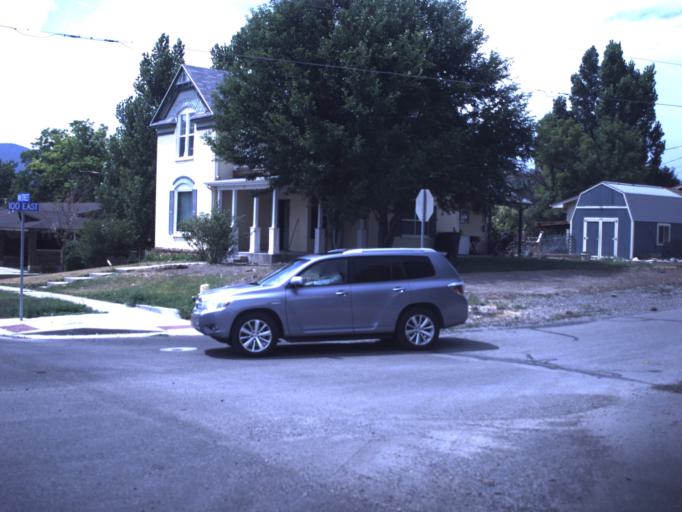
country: US
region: Utah
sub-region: Sanpete County
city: Moroni
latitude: 39.5250
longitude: -111.5819
